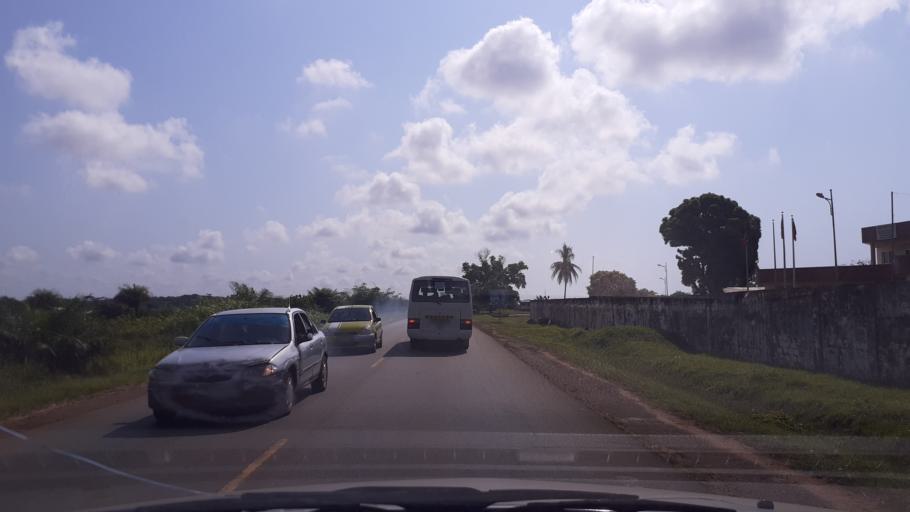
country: LR
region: Montserrado
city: Bensonville City
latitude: 6.2101
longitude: -10.5660
